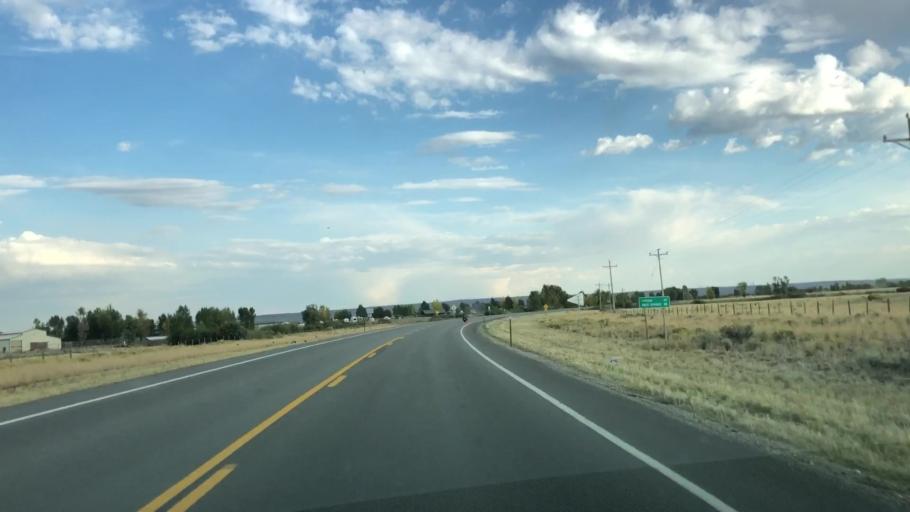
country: US
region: Wyoming
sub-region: Sublette County
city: Pinedale
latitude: 42.7437
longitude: -109.7182
